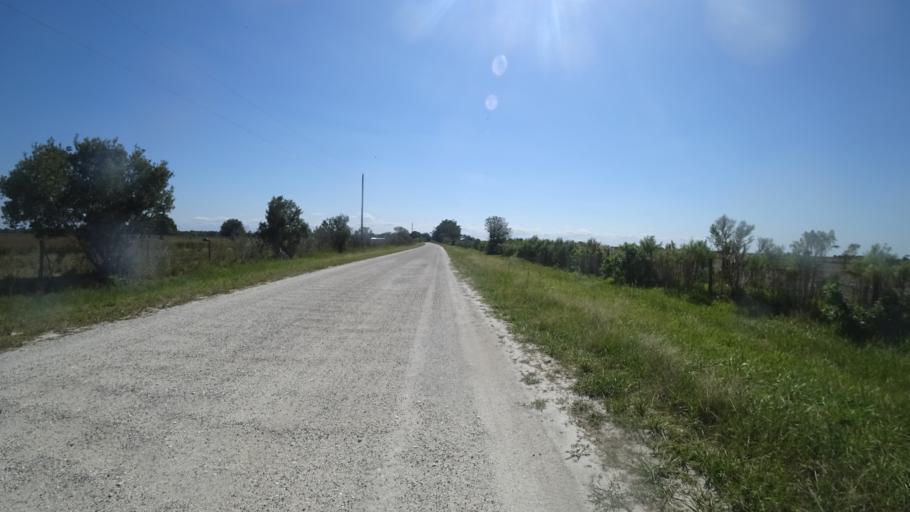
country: US
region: Florida
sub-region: DeSoto County
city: Arcadia
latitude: 27.3292
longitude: -82.0805
